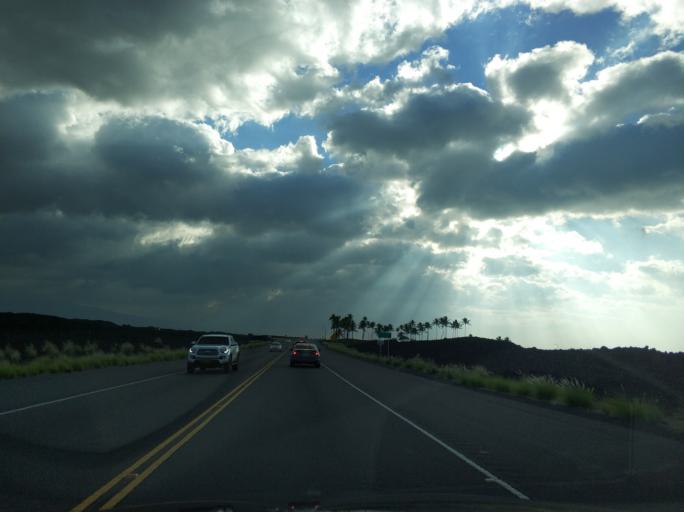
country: US
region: Hawaii
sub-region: Hawaii County
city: Waikoloa Village
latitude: 19.9373
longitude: -155.8407
